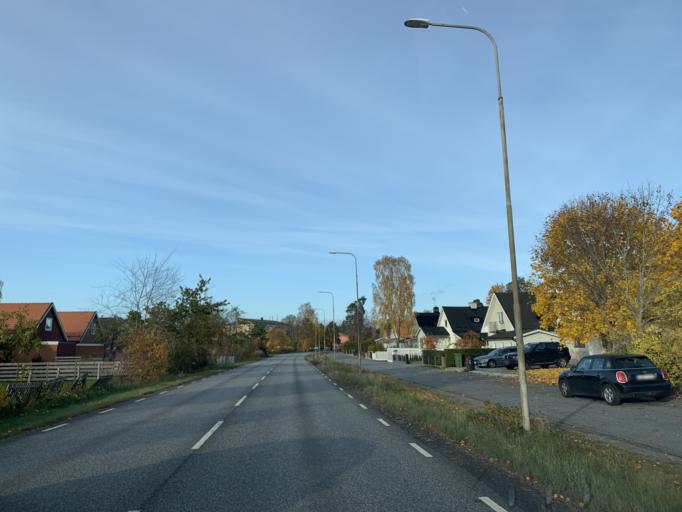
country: SE
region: Stockholm
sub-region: Haninge Kommun
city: Haninge
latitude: 59.1823
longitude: 18.1810
